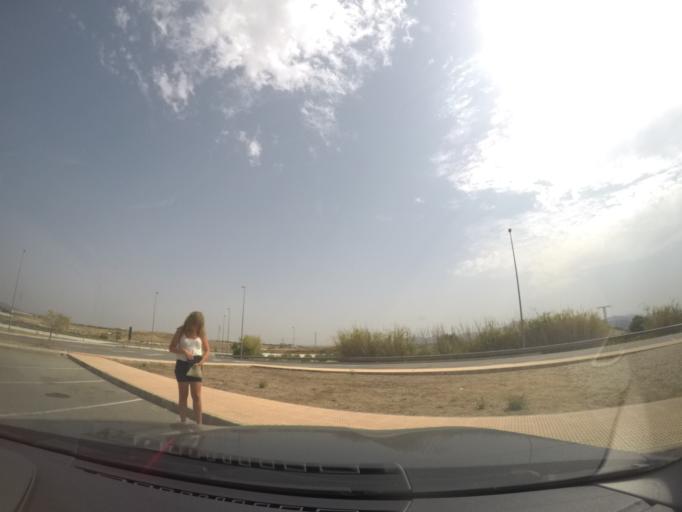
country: ES
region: Murcia
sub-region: Murcia
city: Mazarron
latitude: 37.5932
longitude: -1.3661
